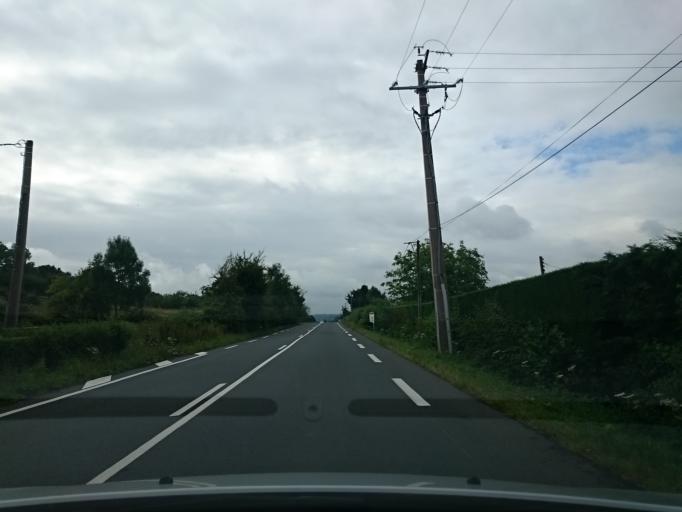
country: FR
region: Lower Normandy
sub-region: Departement du Calvados
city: Beuvillers
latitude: 49.0741
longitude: 0.3251
